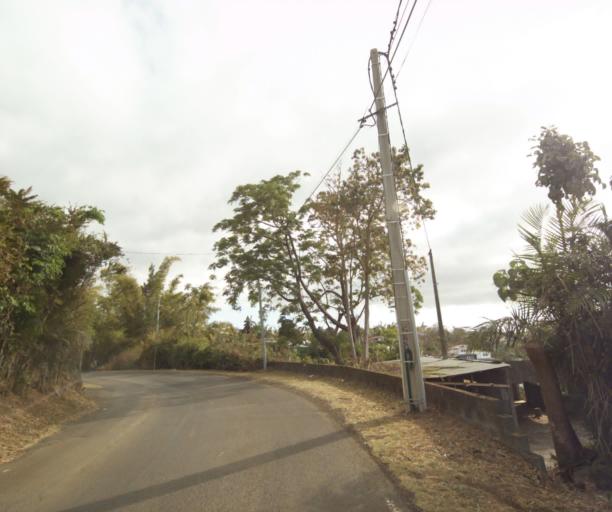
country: RE
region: Reunion
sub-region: Reunion
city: Saint-Paul
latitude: -21.0366
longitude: 55.3075
